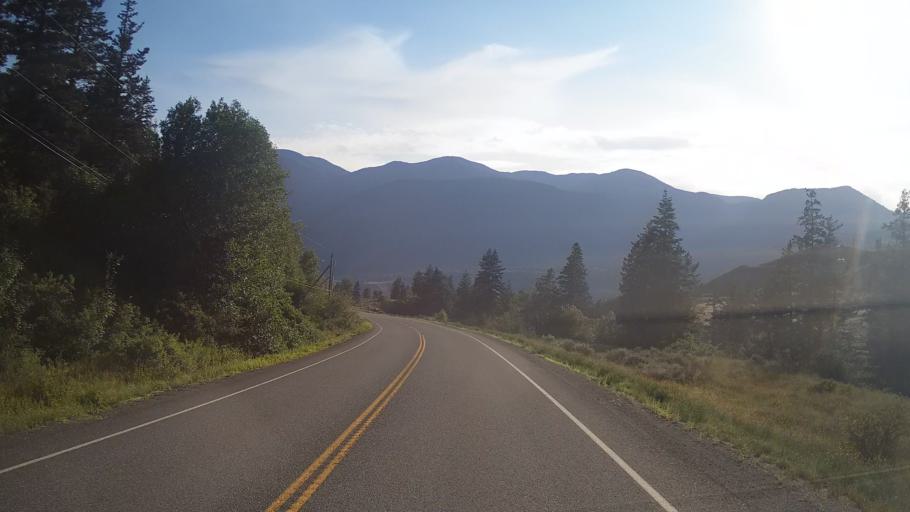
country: CA
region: British Columbia
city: Lillooet
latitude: 50.8685
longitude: -121.8422
